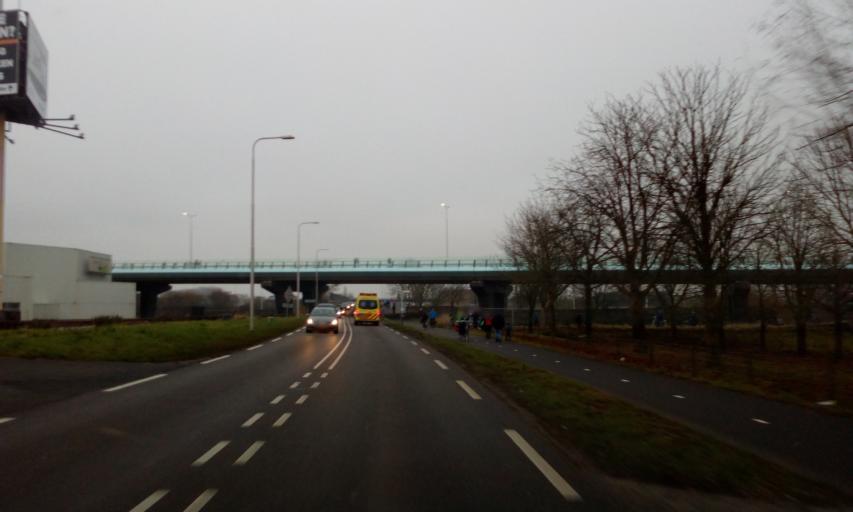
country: NL
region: South Holland
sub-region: Gemeente Waddinxveen
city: Waddinxveen
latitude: 52.0260
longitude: 4.6627
